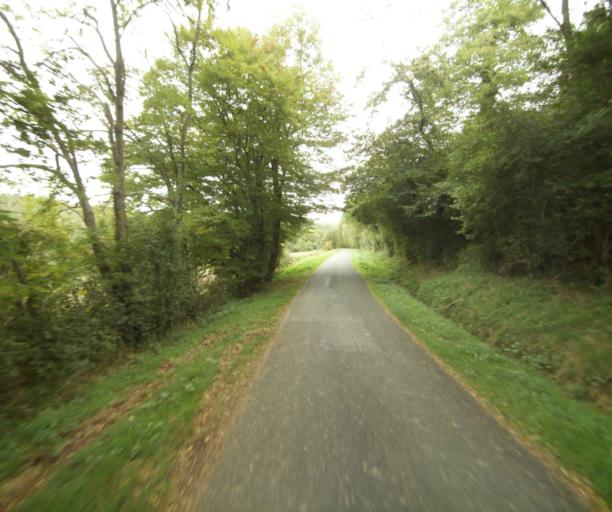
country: FR
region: Midi-Pyrenees
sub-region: Departement du Gers
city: Eauze
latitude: 43.9005
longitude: 0.0622
